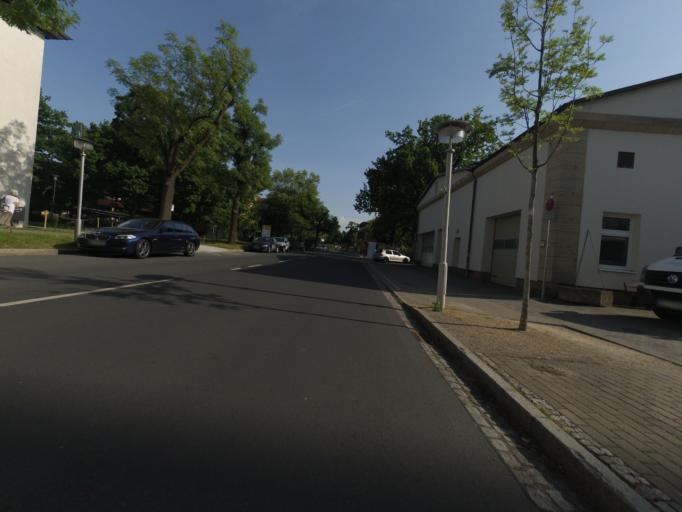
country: DE
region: Saxony
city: Albertstadt
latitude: 51.0556
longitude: 13.7812
